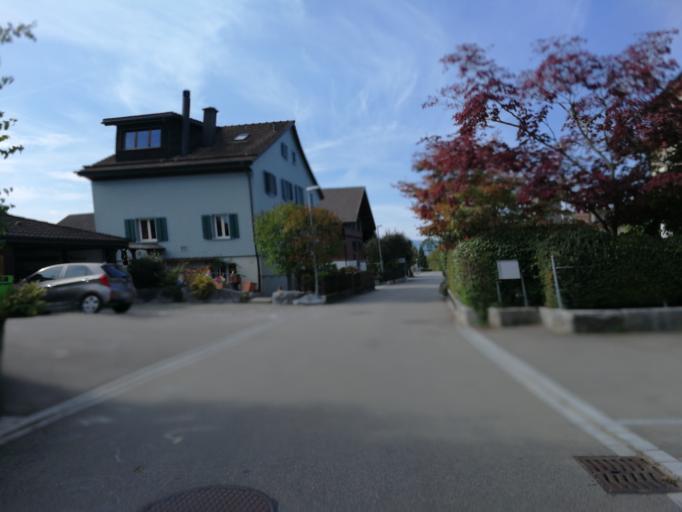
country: CH
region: Zurich
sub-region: Bezirk Meilen
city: Obermeilen
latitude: 47.2632
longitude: 8.6695
